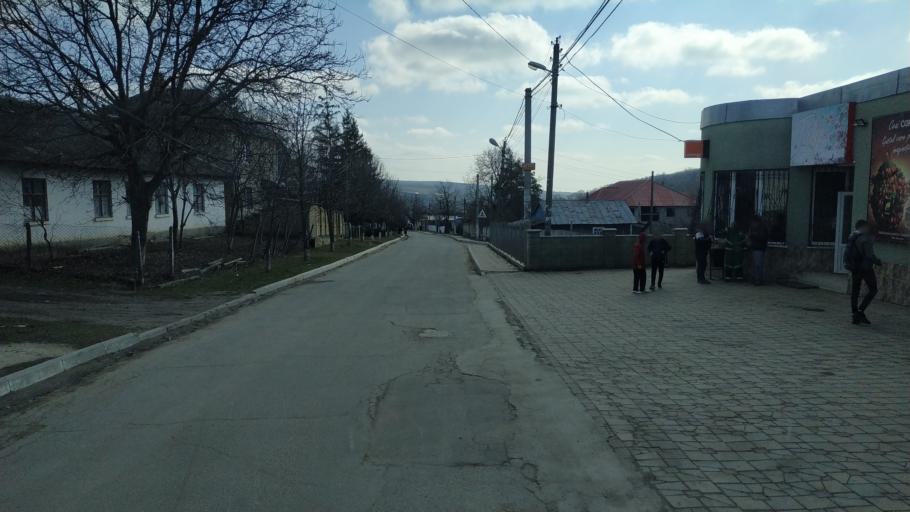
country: MD
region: Hincesti
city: Hincesti
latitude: 46.8265
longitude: 28.6718
